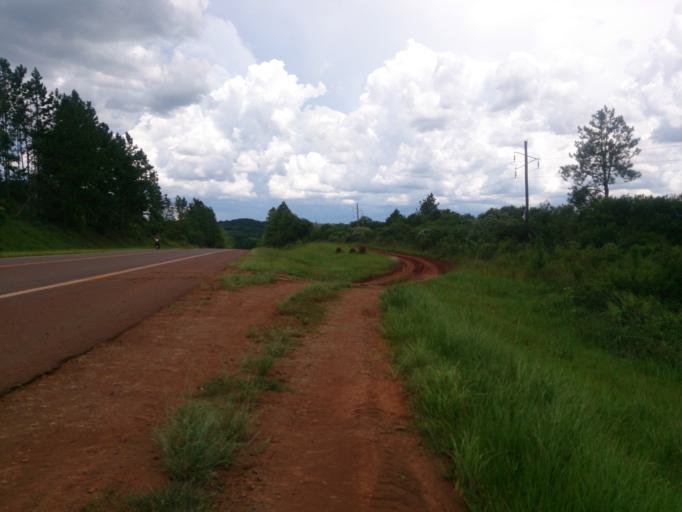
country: AR
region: Misiones
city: Campo Viera
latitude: -27.3603
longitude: -55.0504
